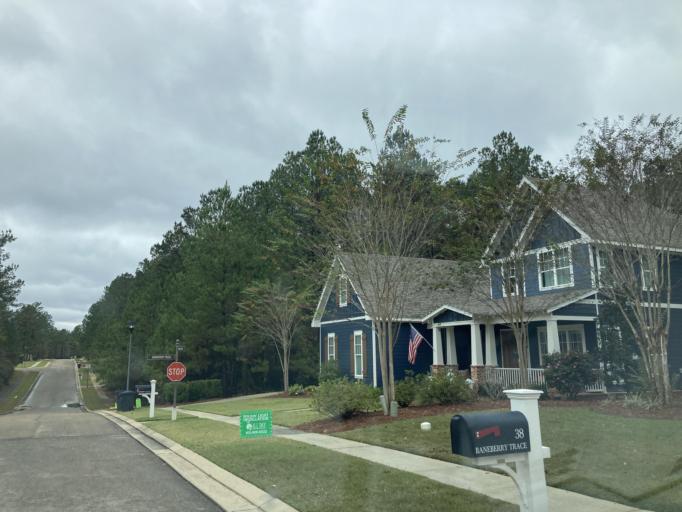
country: US
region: Mississippi
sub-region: Lamar County
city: West Hattiesburg
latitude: 31.2876
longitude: -89.4745
